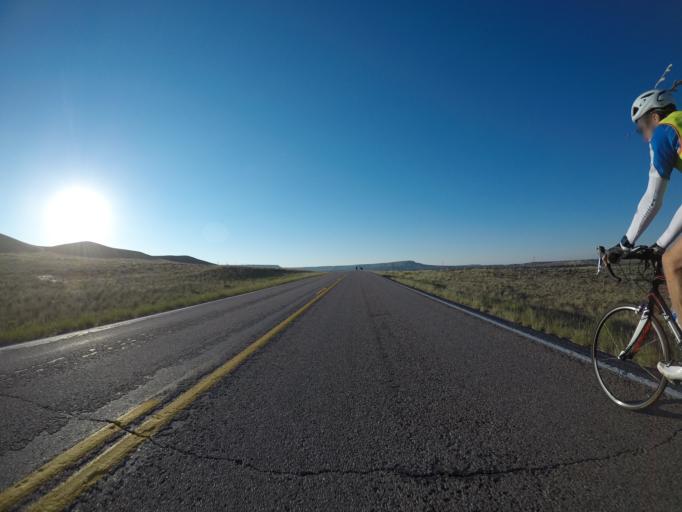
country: US
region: Wyoming
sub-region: Sublette County
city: Marbleton
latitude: 42.5746
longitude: -109.9800
